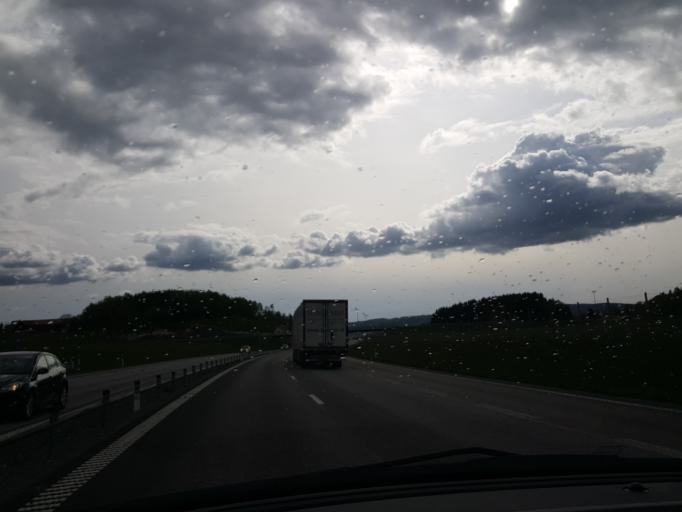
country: SE
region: Vaestra Goetaland
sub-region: Trollhattan
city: Sjuntorp
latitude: 58.2111
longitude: 12.1826
